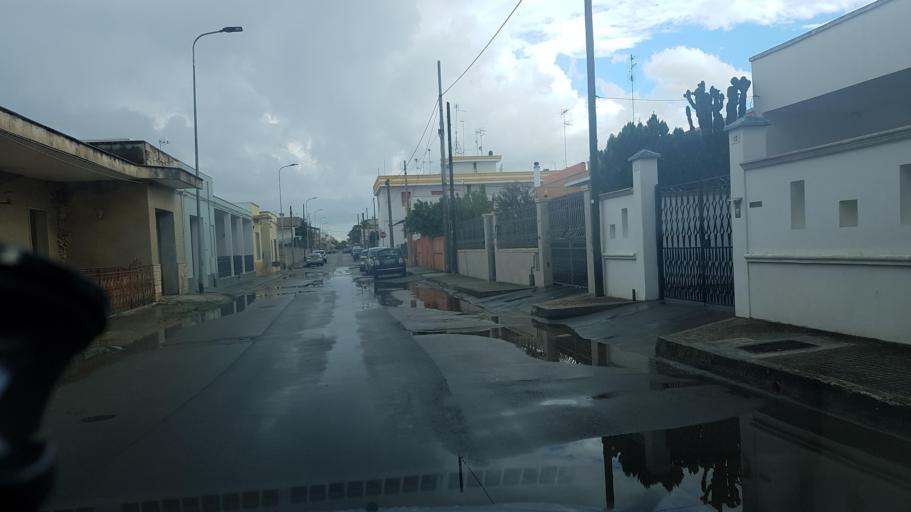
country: IT
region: Apulia
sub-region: Provincia di Lecce
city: Carmiano
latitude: 40.3413
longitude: 18.0411
